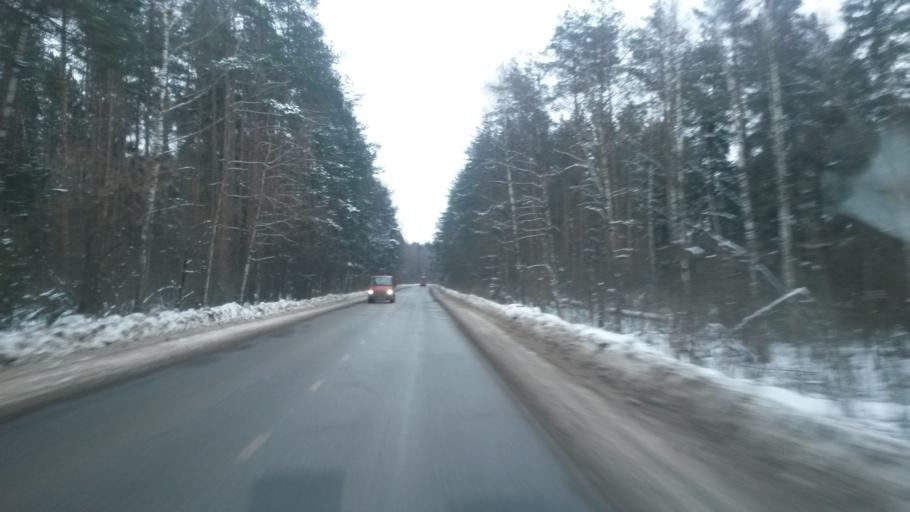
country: RU
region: Ivanovo
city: Kokhma
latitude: 56.9703
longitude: 41.0853
